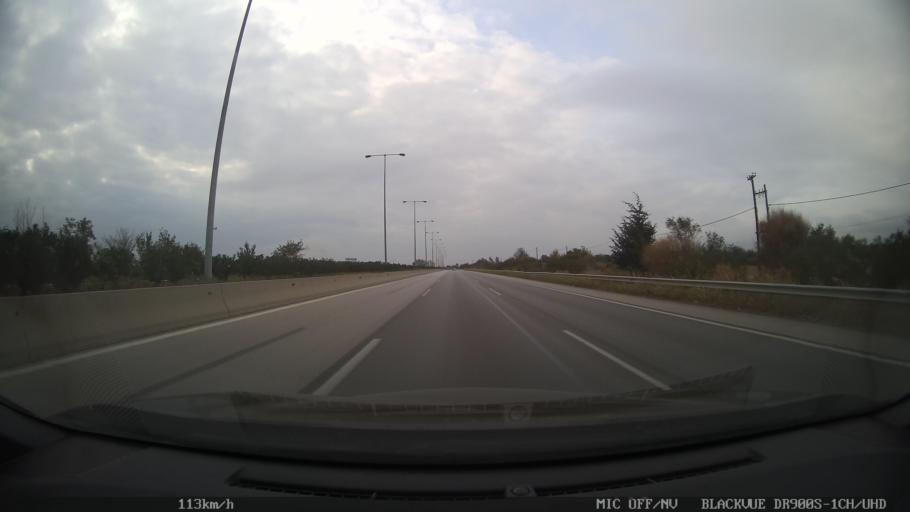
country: GR
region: Central Macedonia
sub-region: Nomos Thessalonikis
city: Nea Magnisia
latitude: 40.6804
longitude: 22.8324
